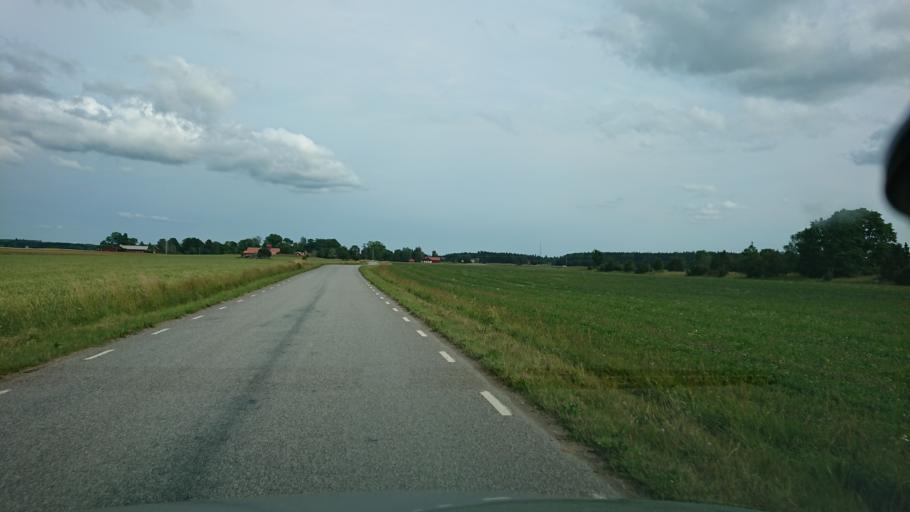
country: SE
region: Uppsala
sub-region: Osthammars Kommun
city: Bjorklinge
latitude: 59.9980
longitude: 17.4894
